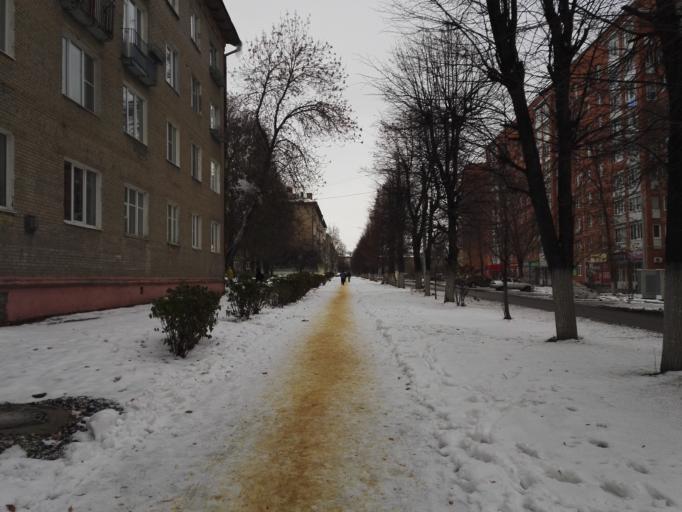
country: RU
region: Tula
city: Novomoskovsk
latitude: 54.0103
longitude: 38.3095
